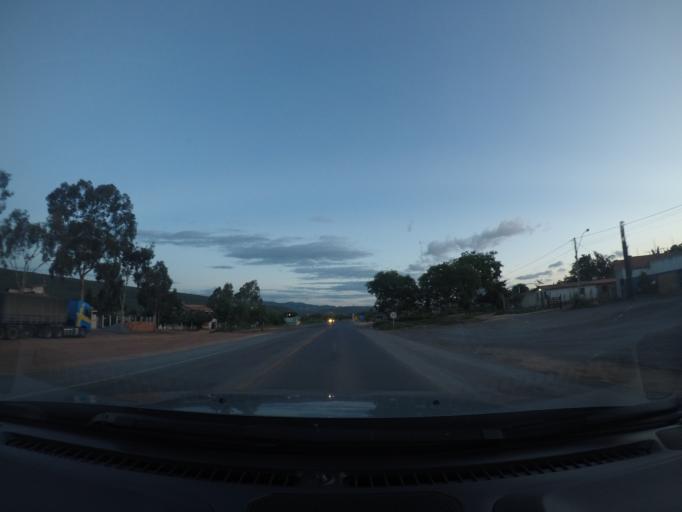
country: BR
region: Bahia
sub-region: Seabra
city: Seabra
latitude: -12.4656
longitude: -41.7448
